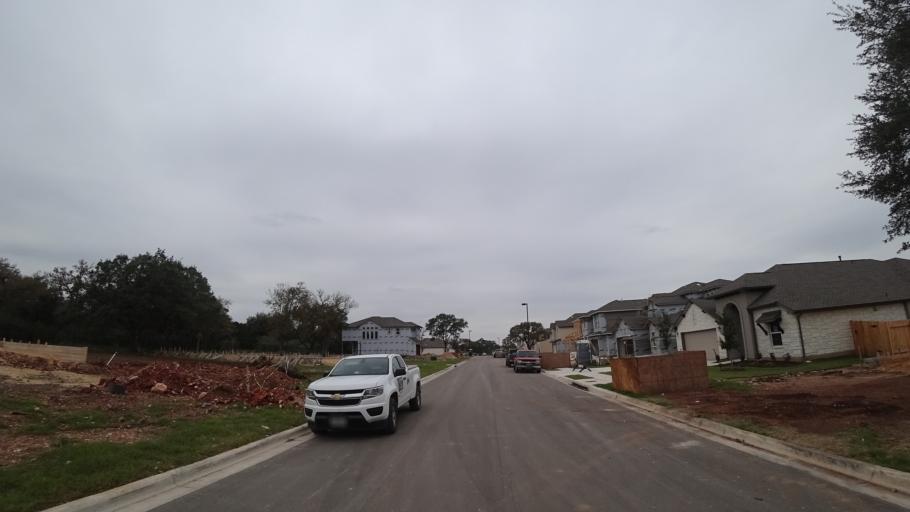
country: US
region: Texas
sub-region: Travis County
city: Shady Hollow
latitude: 30.1654
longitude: -97.8880
